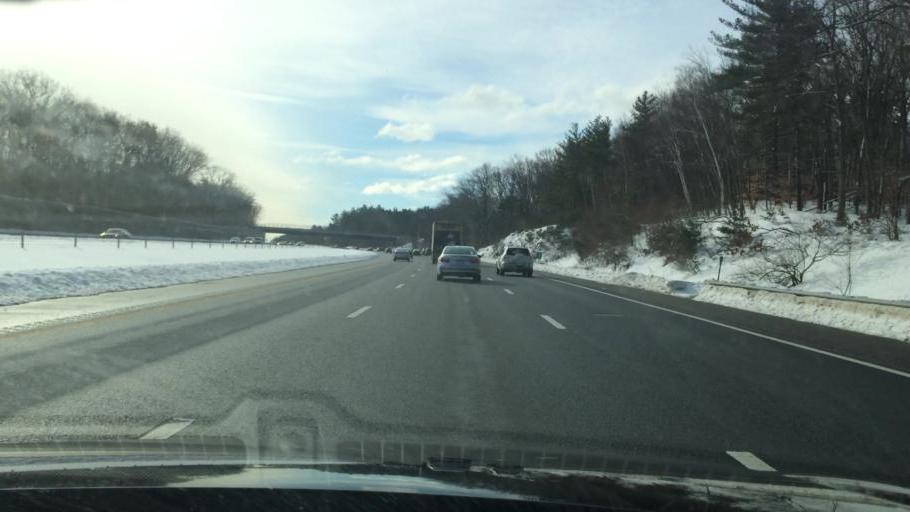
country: US
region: Massachusetts
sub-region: Middlesex County
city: Billerica
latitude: 42.5322
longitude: -71.2767
